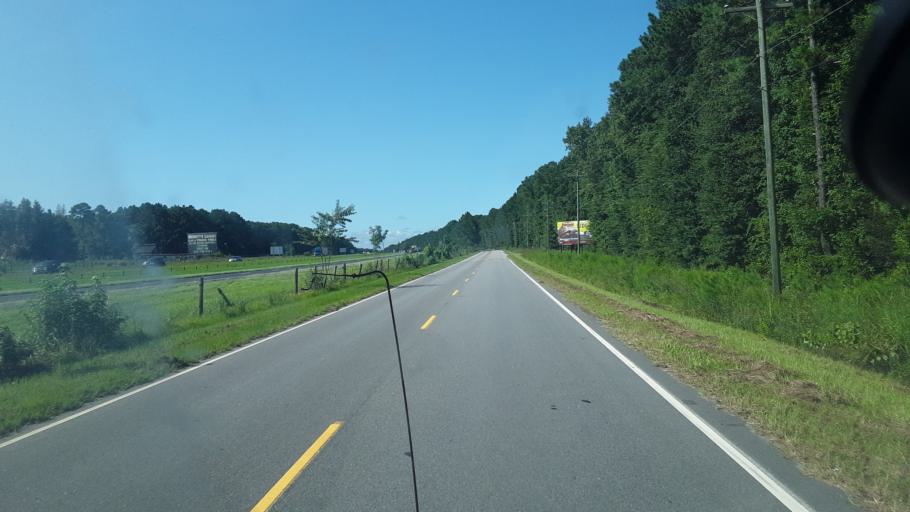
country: US
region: South Carolina
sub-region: Hampton County
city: Yemassee
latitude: 32.6220
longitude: -80.8890
